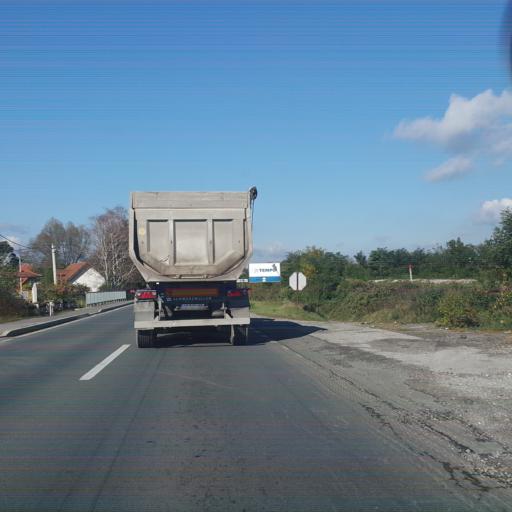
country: RS
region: Central Serbia
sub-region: Raski Okrug
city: Vrnjacka Banja
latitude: 43.6367
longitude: 20.9327
